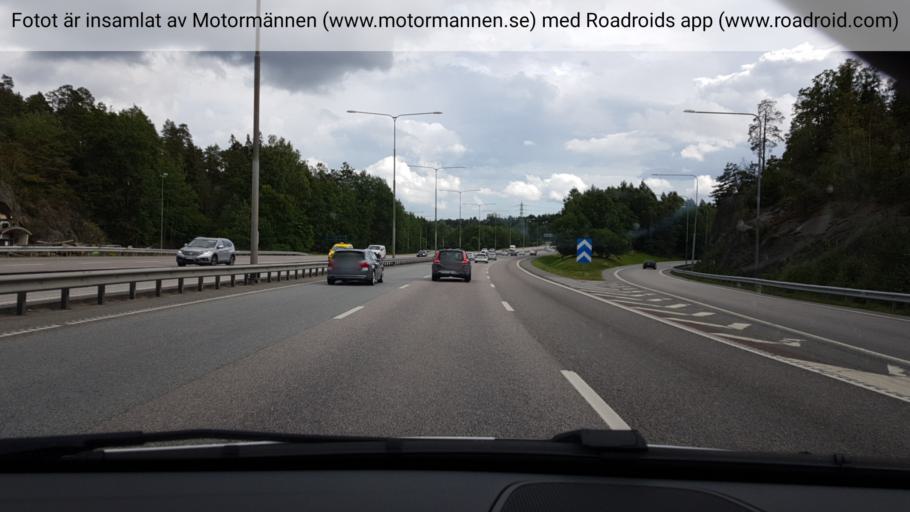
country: SE
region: Stockholm
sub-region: Haninge Kommun
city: Handen
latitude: 59.2227
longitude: 18.1316
